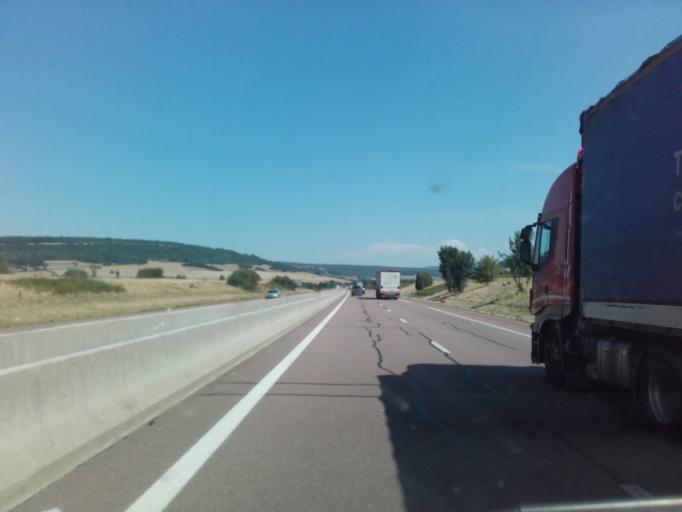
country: FR
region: Bourgogne
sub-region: Departement de la Cote-d'Or
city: Pouilly-en-Auxois
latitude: 47.2079
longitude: 4.6239
